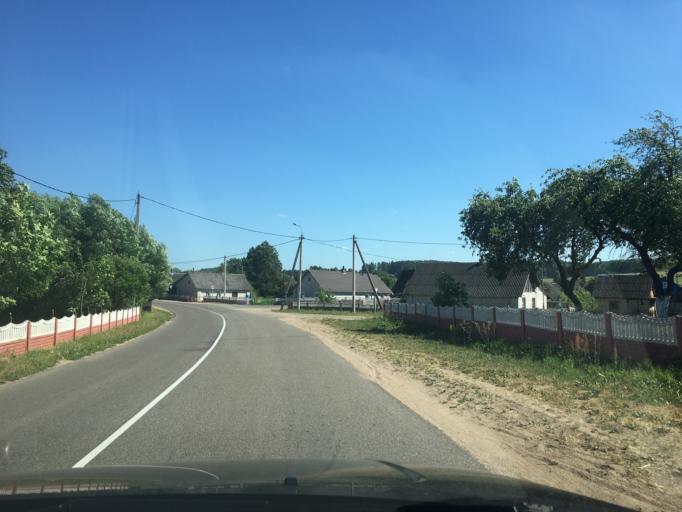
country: BY
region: Grodnenskaya
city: Hal'shany
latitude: 54.2606
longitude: 25.9962
